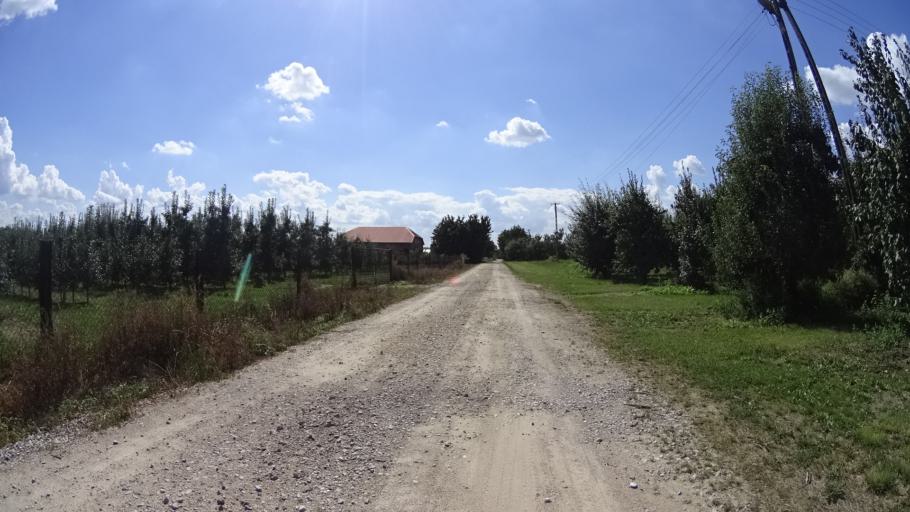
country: PL
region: Masovian Voivodeship
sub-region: Powiat grojecki
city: Mogielnica
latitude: 51.6844
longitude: 20.7677
